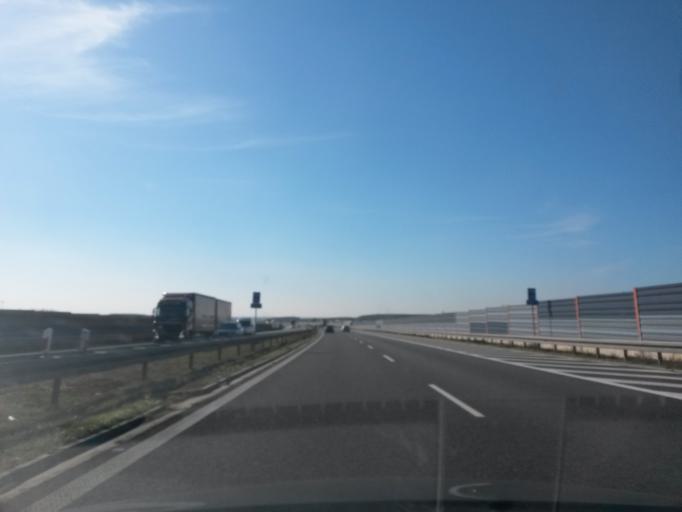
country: PL
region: Opole Voivodeship
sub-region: Powiat krapkowicki
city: Gogolin
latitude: 50.4836
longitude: 18.0387
